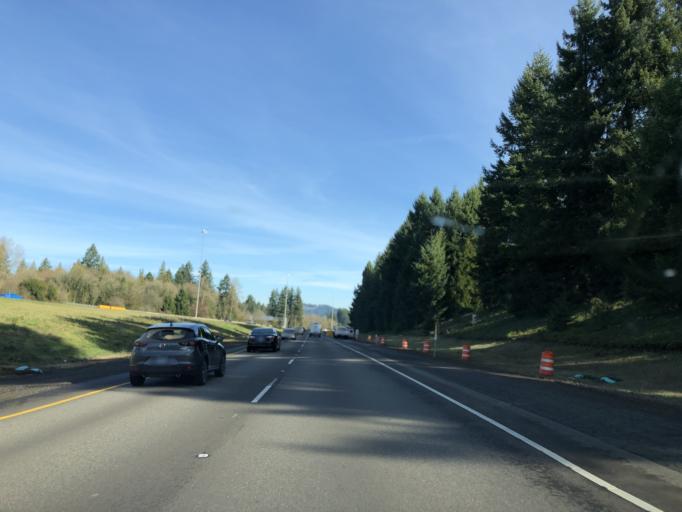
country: US
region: Oregon
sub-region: Washington County
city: Tualatin
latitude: 45.3683
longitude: -122.7534
